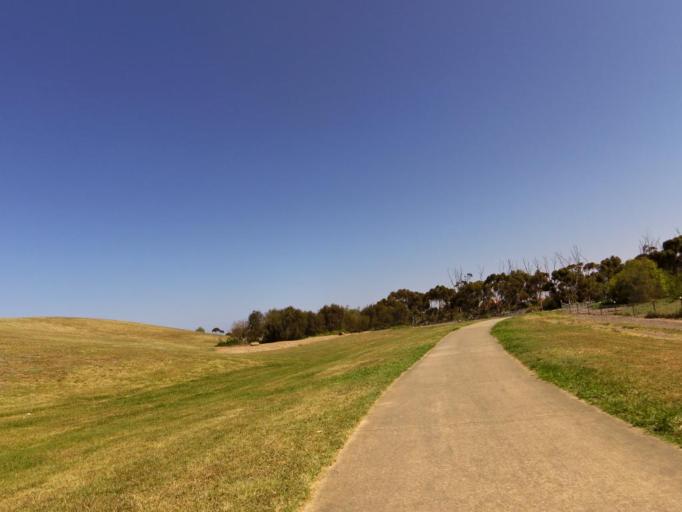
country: AU
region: Victoria
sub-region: Hobsons Bay
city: Altona Meadows
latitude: -37.8824
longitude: 144.7960
